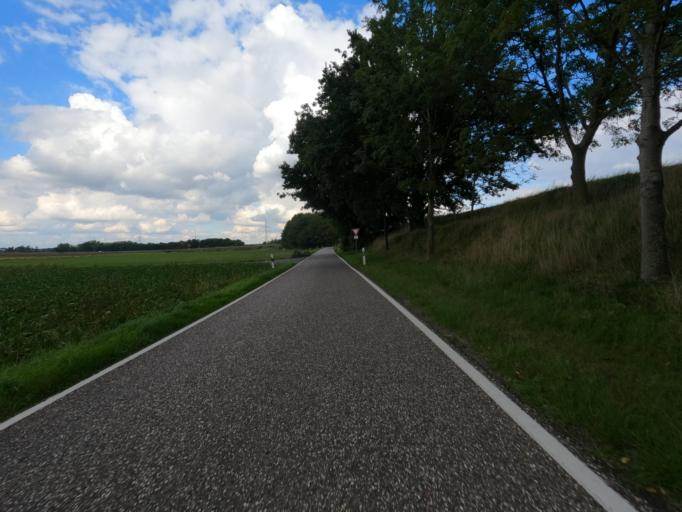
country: DE
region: North Rhine-Westphalia
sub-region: Regierungsbezirk Koln
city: Aldenhoven
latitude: 50.9197
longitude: 6.3068
